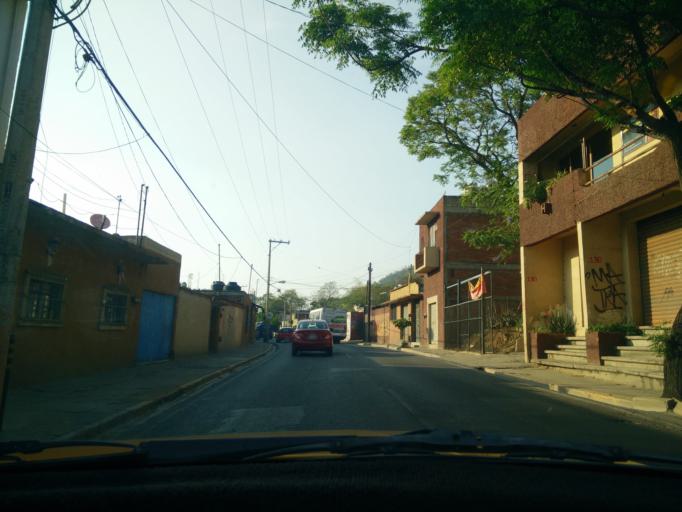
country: MX
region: Oaxaca
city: Oaxaca de Juarez
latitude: 17.0705
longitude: -96.7365
